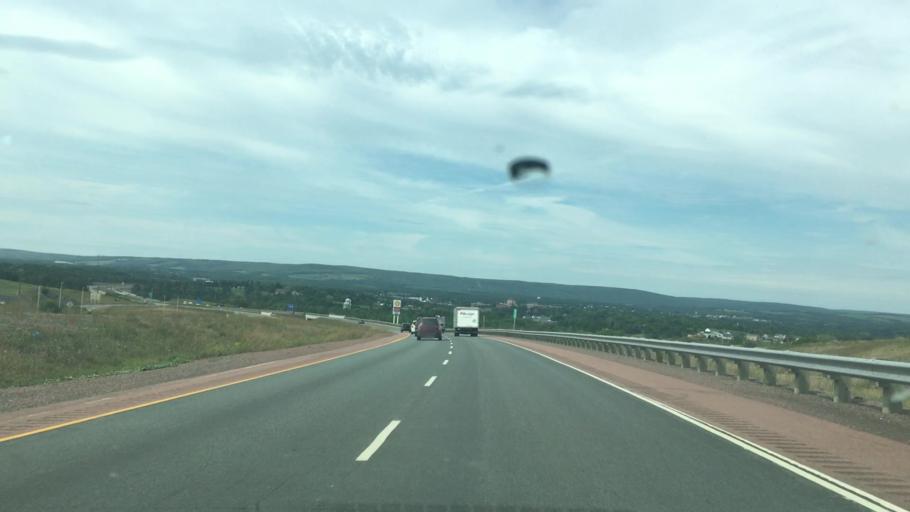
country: CA
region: Nova Scotia
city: Antigonish
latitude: 45.6094
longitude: -61.9627
